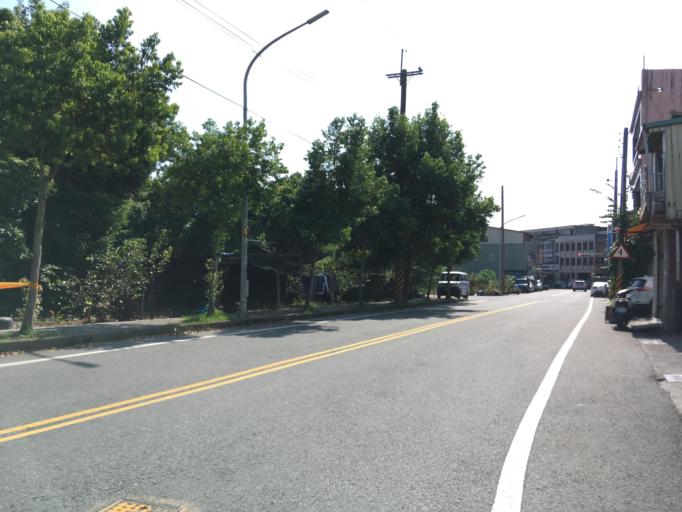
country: TW
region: Taiwan
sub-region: Yilan
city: Yilan
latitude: 24.6676
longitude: 121.6546
